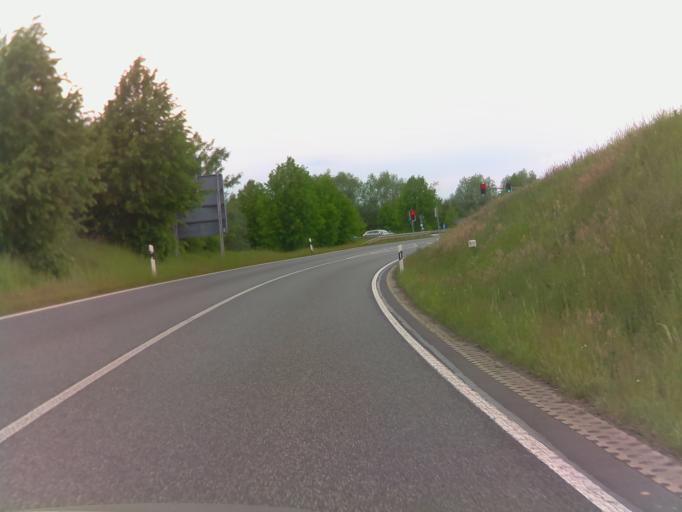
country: DE
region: Hesse
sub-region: Regierungsbezirk Kassel
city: Schrecksbach
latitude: 50.8815
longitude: 9.2659
